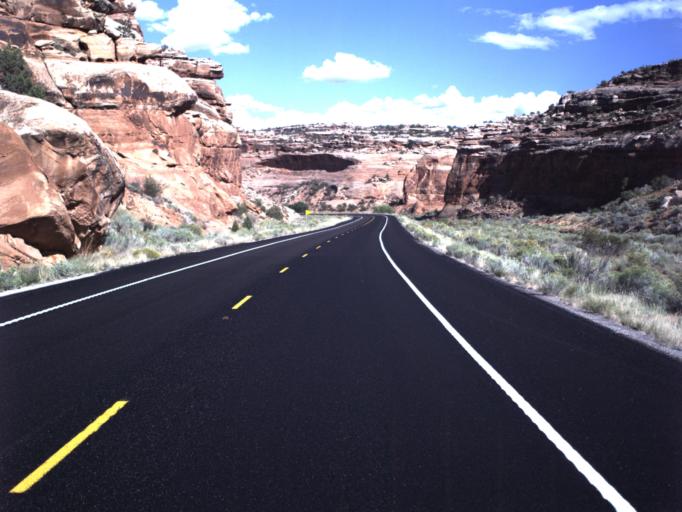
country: US
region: Utah
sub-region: Grand County
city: Moab
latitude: 38.6482
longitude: -109.7296
